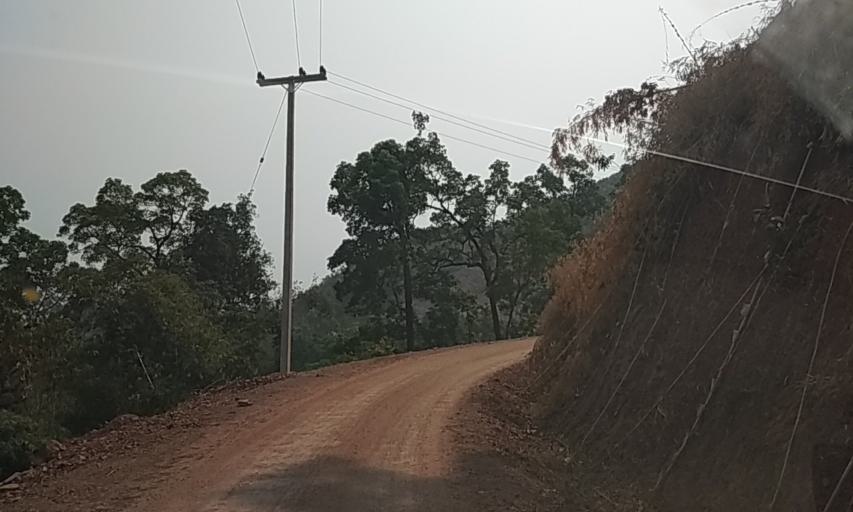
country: VN
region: Huyen Dien Bien
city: Dien Bien Phu
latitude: 21.4863
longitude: 102.7790
